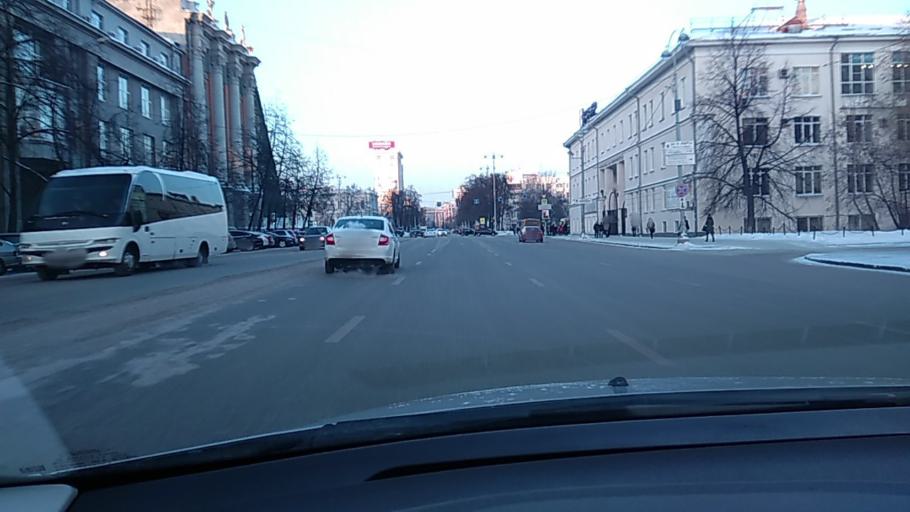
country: RU
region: Sverdlovsk
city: Yekaterinburg
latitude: 56.8366
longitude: 60.5993
